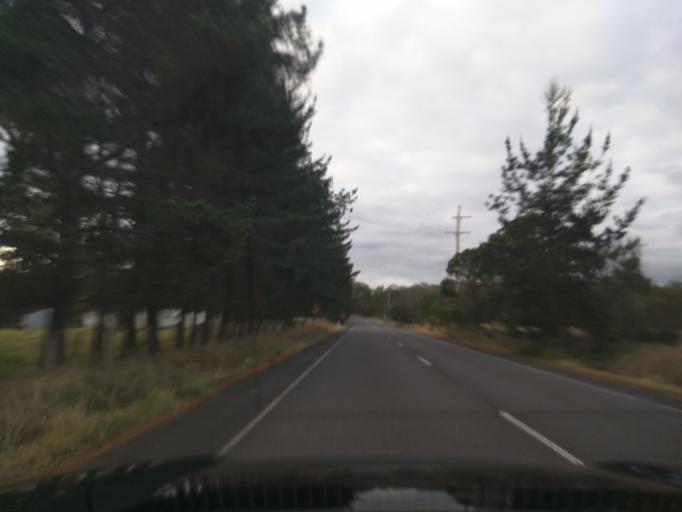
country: AU
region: New South Wales
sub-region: Wollondilly
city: Douglas Park
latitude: -34.2555
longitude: 150.7228
